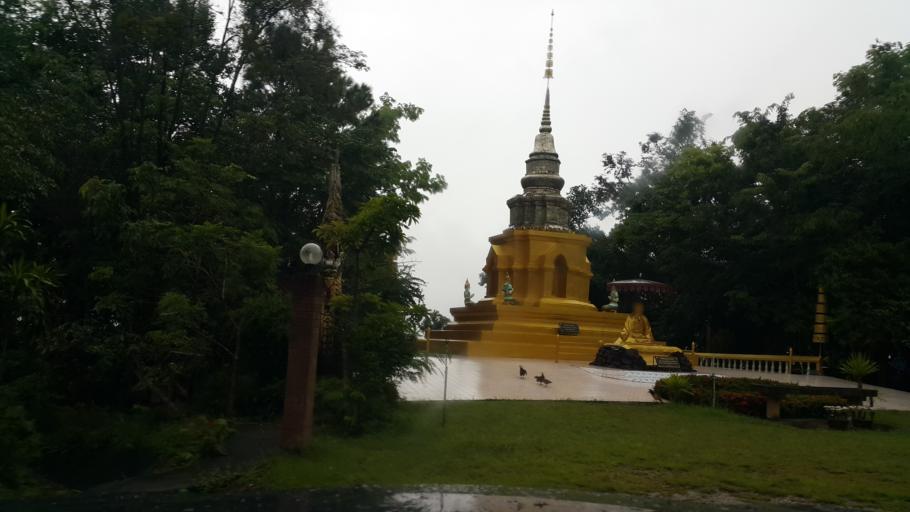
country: TH
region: Phayao
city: Phu Sang
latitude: 19.6042
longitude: 100.4120
